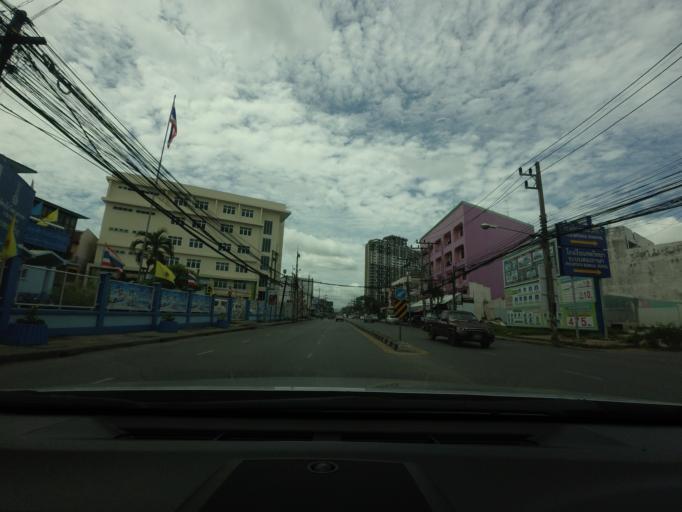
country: TH
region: Songkhla
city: Hat Yai
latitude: 7.0066
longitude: 100.4604
